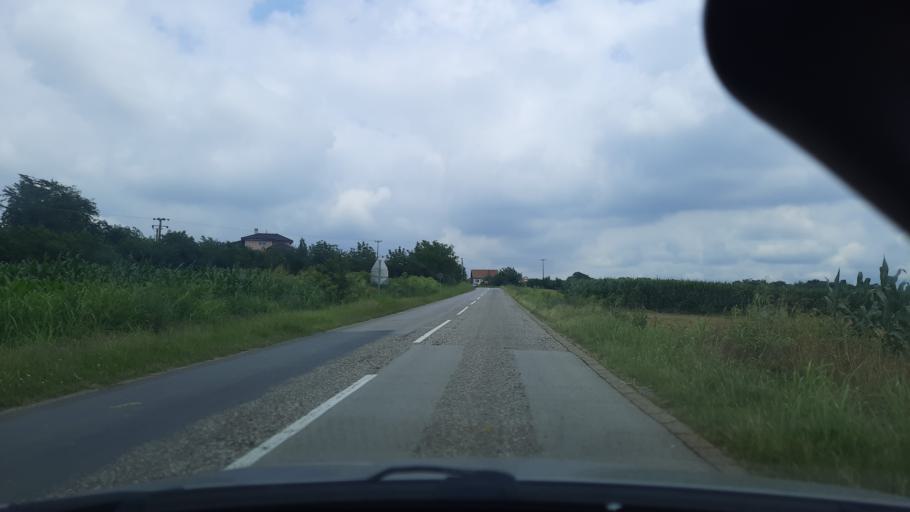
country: RS
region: Central Serbia
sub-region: Branicevski Okrug
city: Malo Crnice
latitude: 44.5739
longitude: 21.3548
